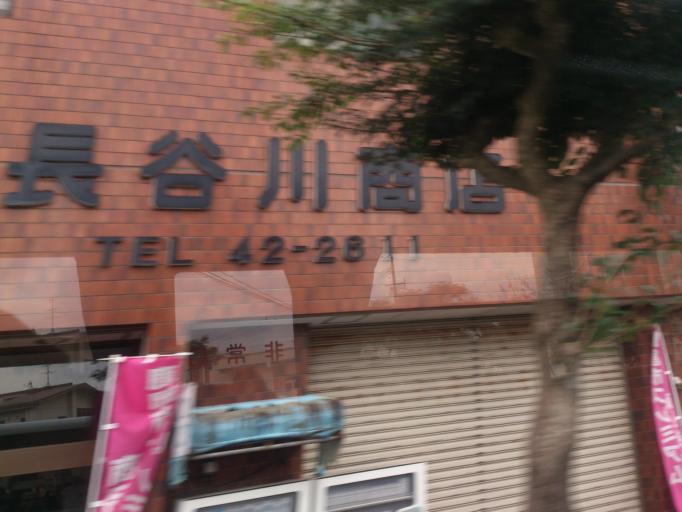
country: JP
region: Kagoshima
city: Kanoya
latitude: 31.3921
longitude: 130.8525
